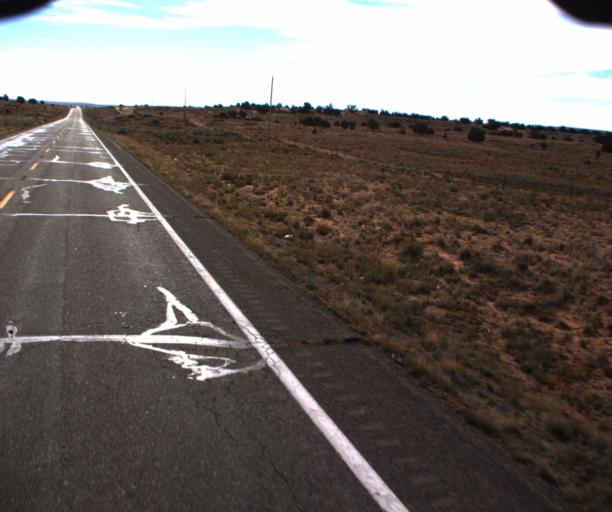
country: US
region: Arizona
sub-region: Coconino County
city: Kaibito
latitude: 36.6192
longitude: -111.1965
